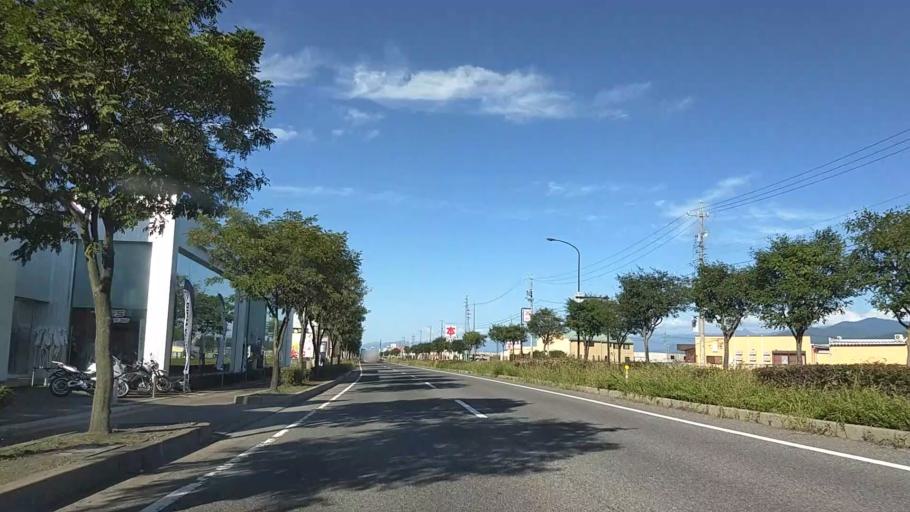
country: JP
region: Nagano
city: Nagano-shi
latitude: 36.5670
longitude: 138.1480
